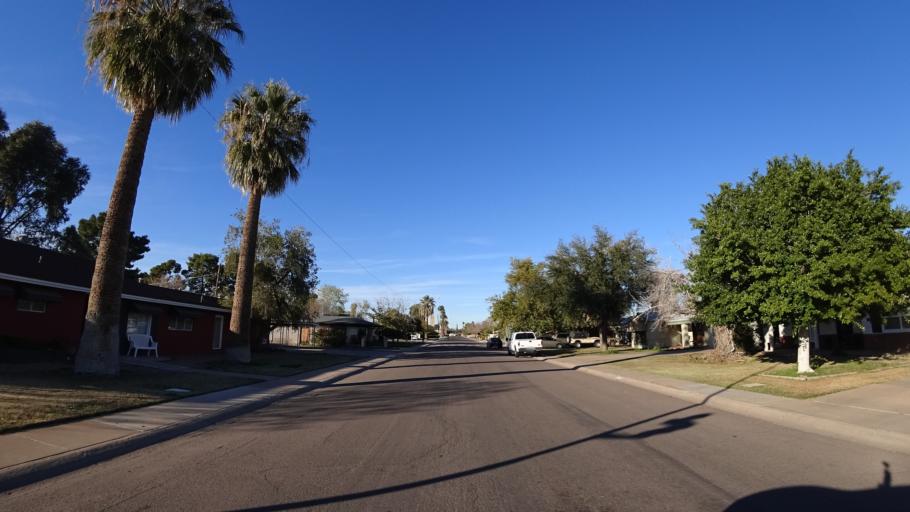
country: US
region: Arizona
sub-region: Maricopa County
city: Phoenix
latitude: 33.4825
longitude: -112.0979
